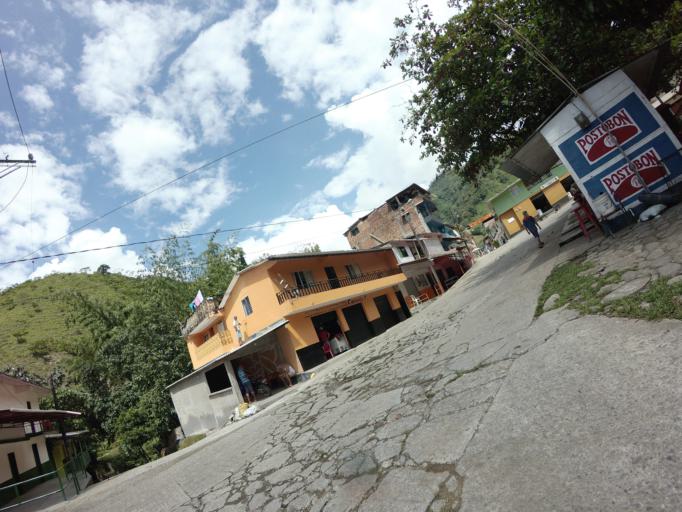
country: CO
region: Antioquia
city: Narino
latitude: 5.5206
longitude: -75.1932
